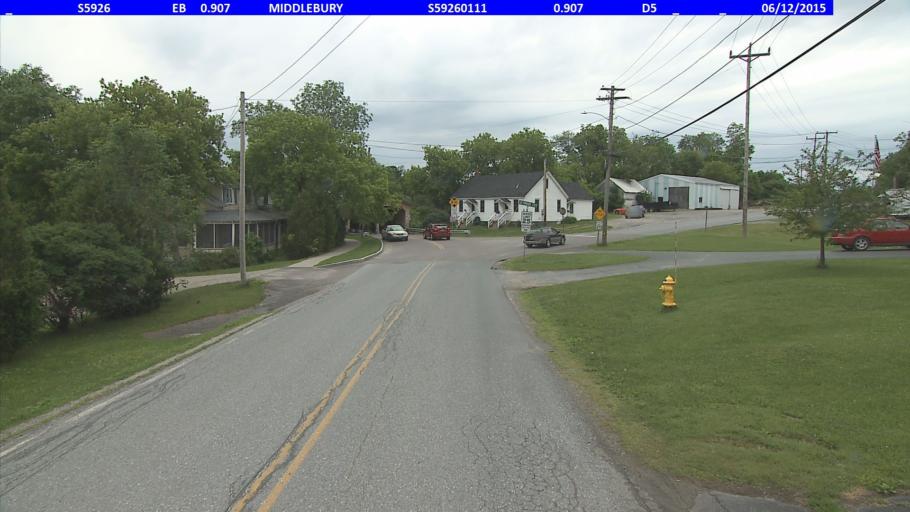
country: US
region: Vermont
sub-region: Addison County
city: Middlebury (village)
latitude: 44.0244
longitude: -73.1763
